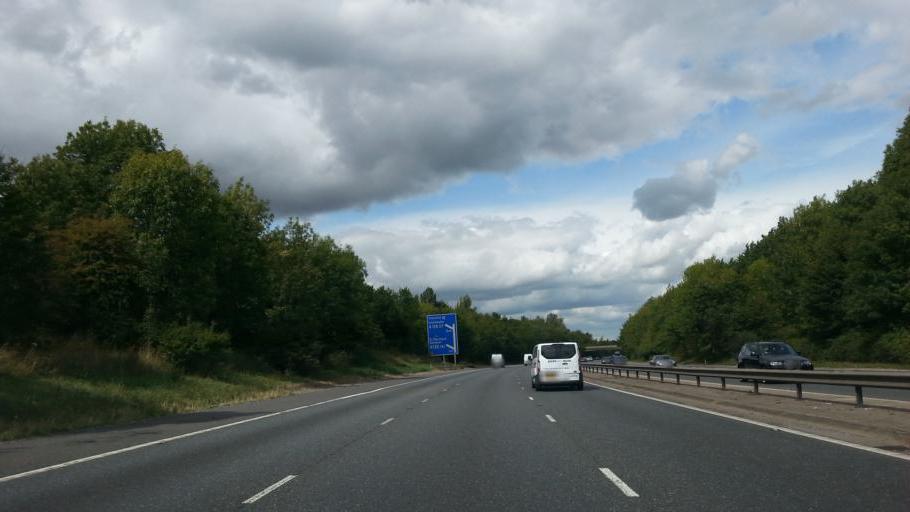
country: GB
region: England
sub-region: Essex
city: Little Hallingbury
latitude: 51.8461
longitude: 0.1865
